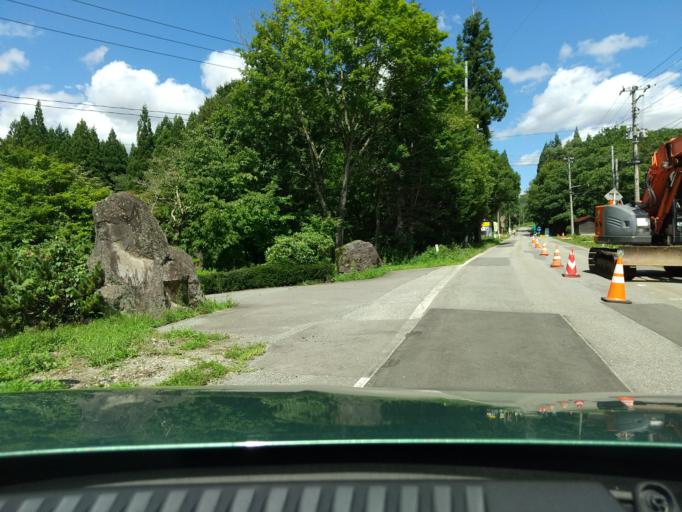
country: JP
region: Akita
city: Kakunodatemachi
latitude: 39.7521
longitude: 140.7258
